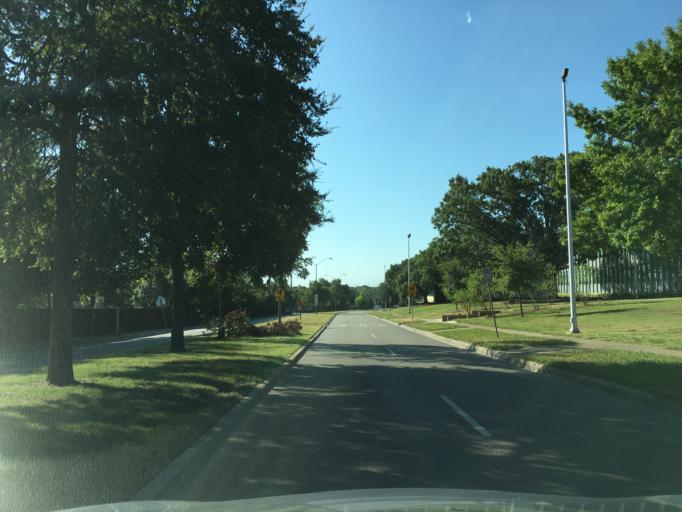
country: US
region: Texas
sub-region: Dallas County
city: Garland
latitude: 32.8572
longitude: -96.7045
